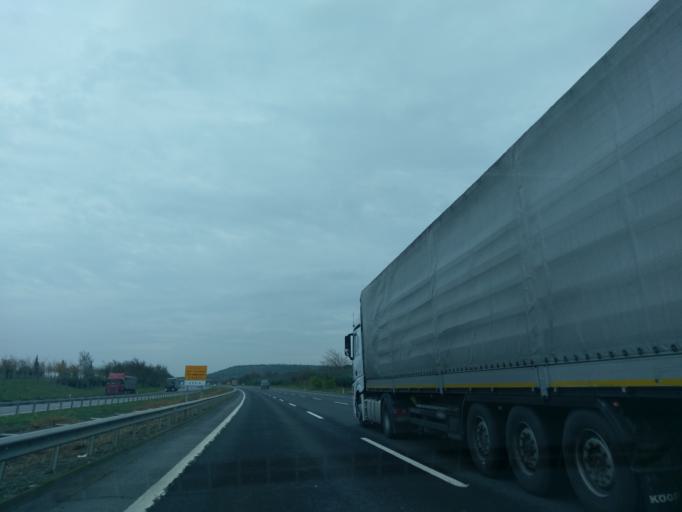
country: TR
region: Istanbul
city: Canta
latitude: 41.1557
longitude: 28.1419
